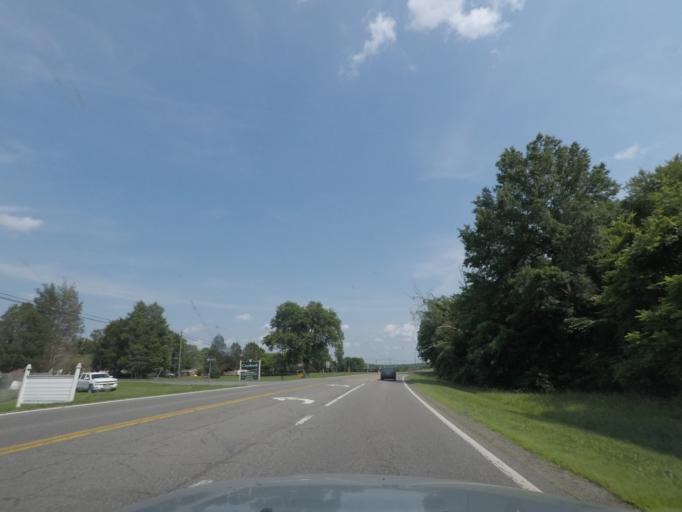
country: US
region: Virginia
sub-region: Fluvanna County
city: Palmyra
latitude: 37.8117
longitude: -78.2420
